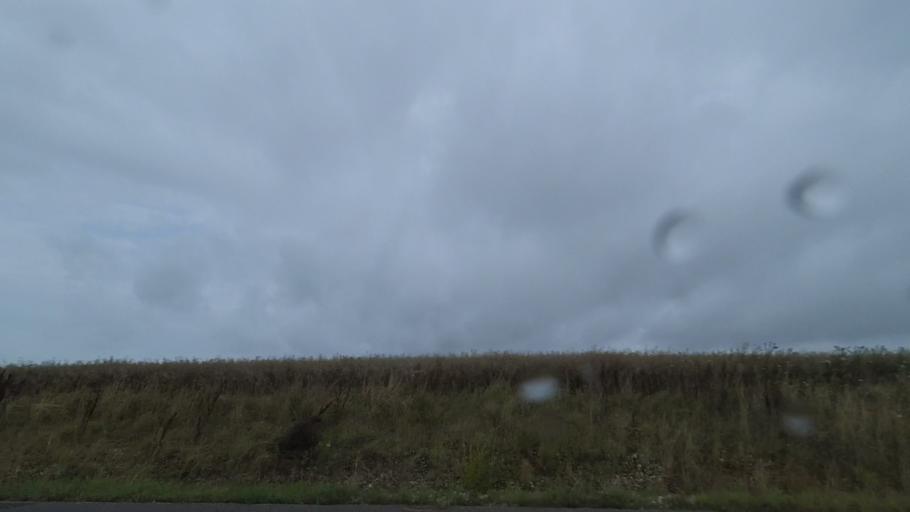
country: DK
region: Central Jutland
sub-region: Syddjurs Kommune
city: Ronde
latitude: 56.3198
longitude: 10.4596
